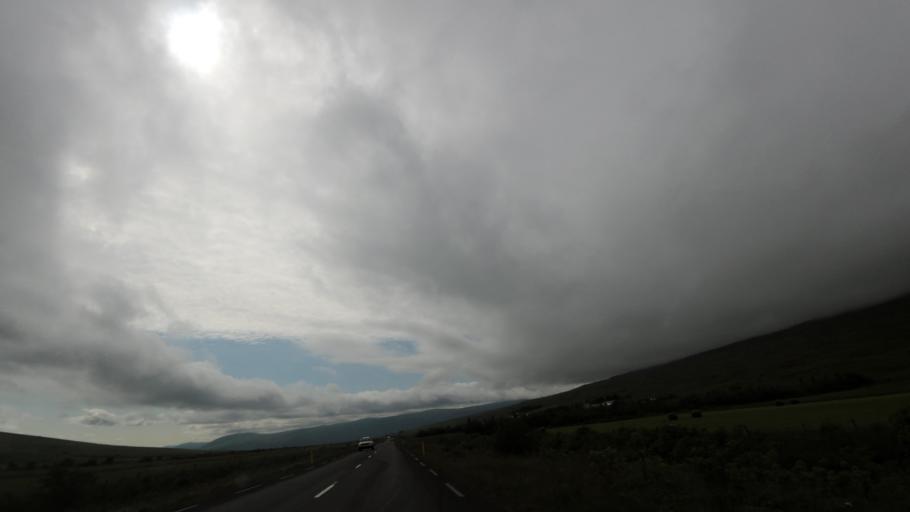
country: IS
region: Northeast
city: Laugar
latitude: 65.7522
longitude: -17.5870
